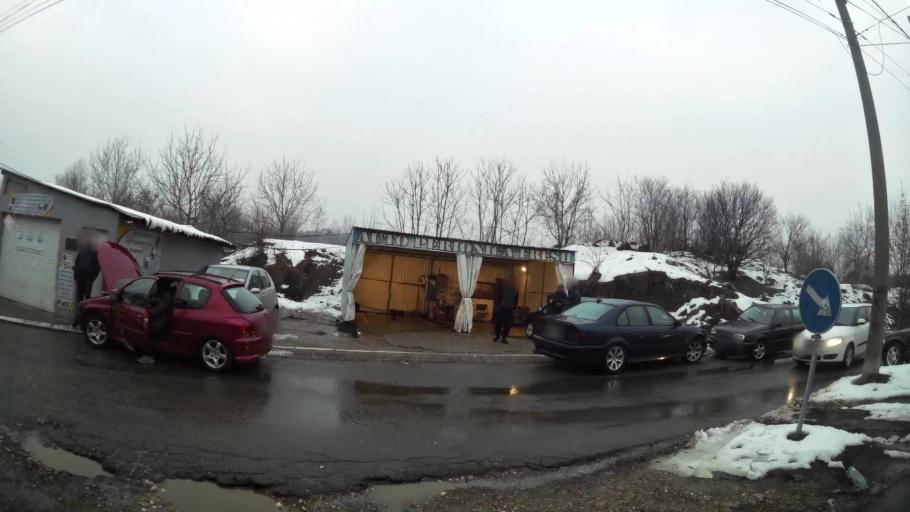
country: RS
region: Central Serbia
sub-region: Belgrade
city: Vozdovac
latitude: 44.7789
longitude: 20.4943
